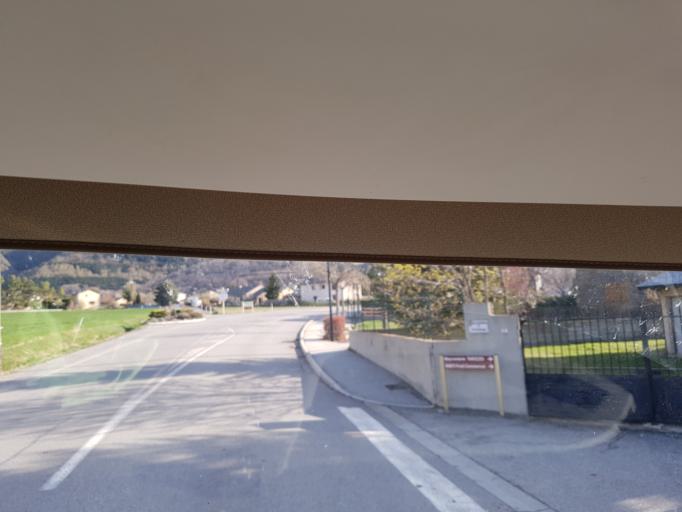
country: ES
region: Catalonia
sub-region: Provincia de Girona
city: Llivia
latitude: 42.4444
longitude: 2.0323
